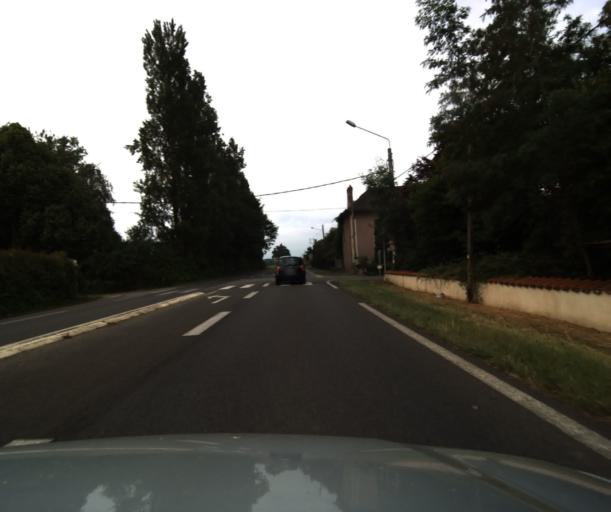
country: FR
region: Midi-Pyrenees
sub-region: Departement des Hautes-Pyrenees
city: Rabastens-de-Bigorre
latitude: 43.3393
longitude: 0.1324
